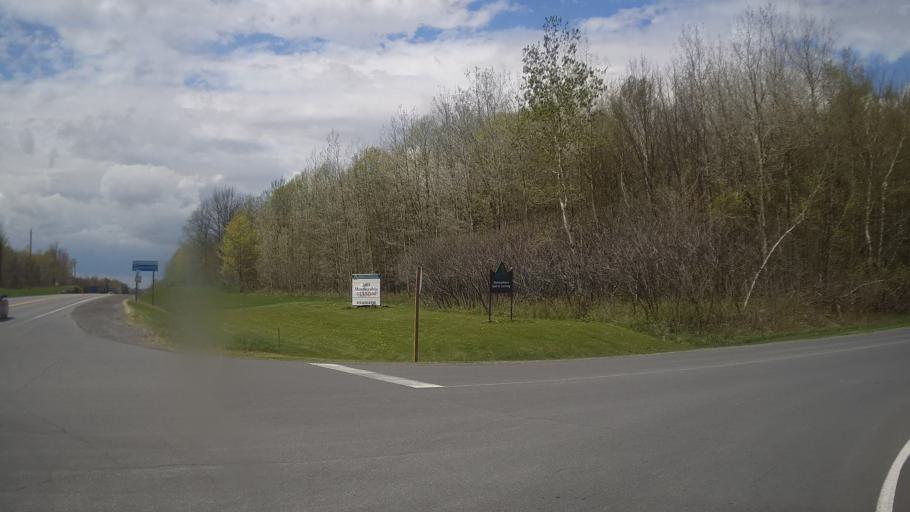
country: CA
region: Ontario
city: Hawkesbury
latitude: 45.5715
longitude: -74.5236
